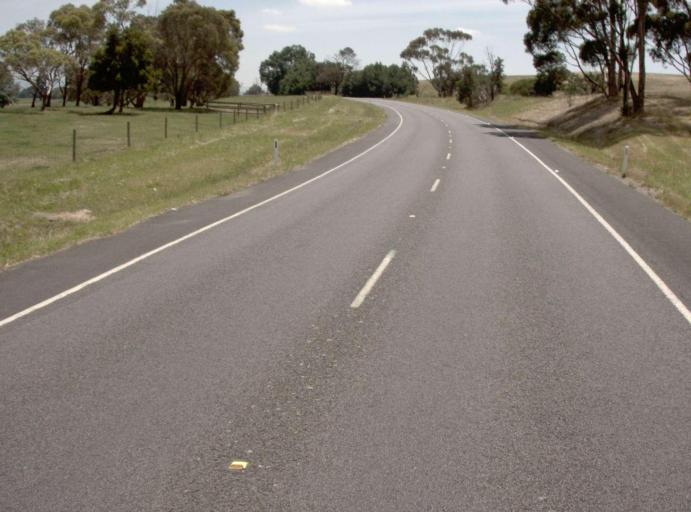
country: AU
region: Victoria
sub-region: Latrobe
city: Traralgon
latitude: -38.2203
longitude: 146.5463
